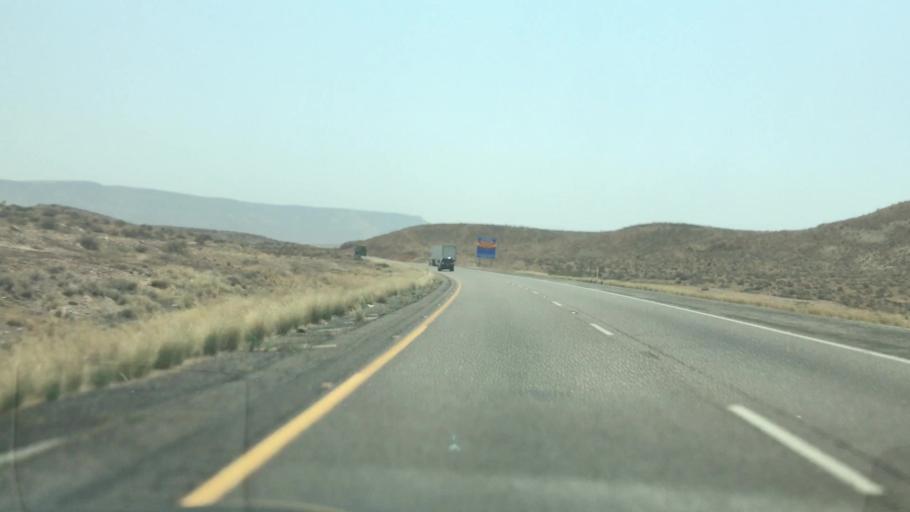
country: US
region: Utah
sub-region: Washington County
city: Saint George
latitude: 36.9999
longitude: -113.6243
